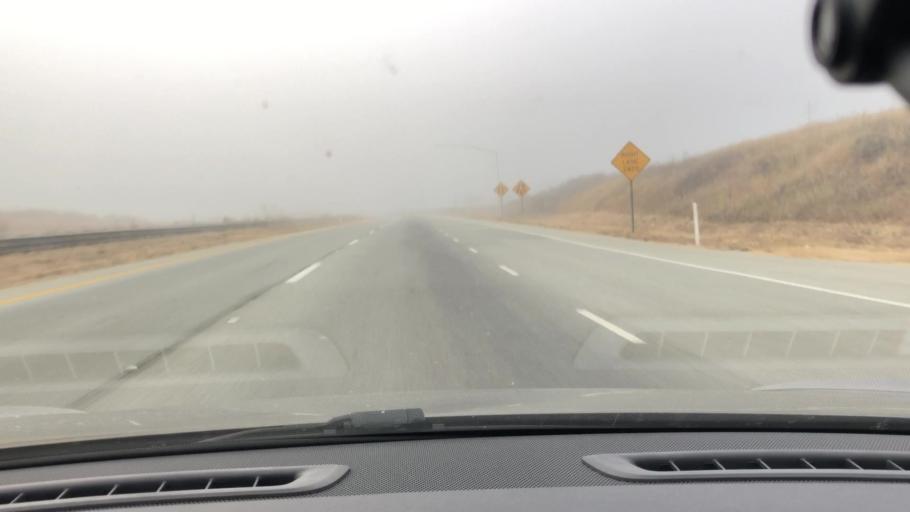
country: US
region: California
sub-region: Monterey County
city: Las Lomas
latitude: 36.8685
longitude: -121.7712
